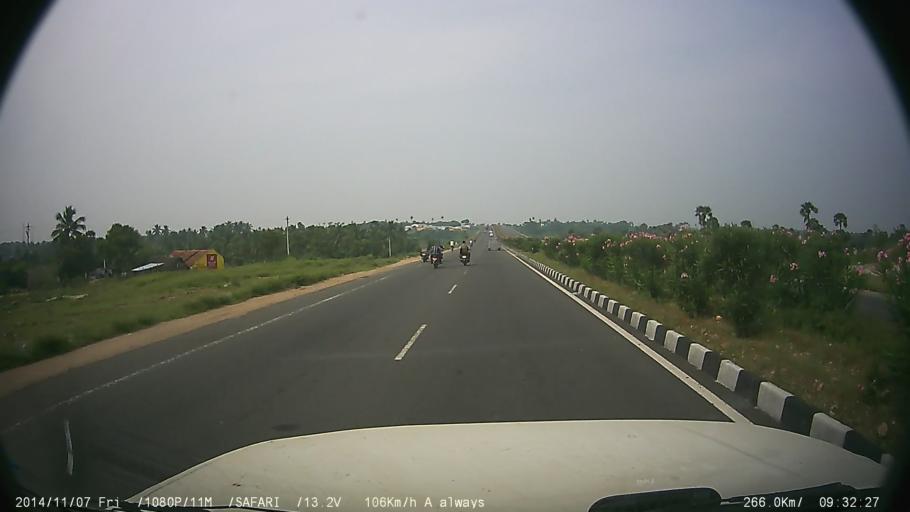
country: IN
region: Tamil Nadu
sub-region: Erode
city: Bhavani
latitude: 11.4093
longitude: 77.6647
